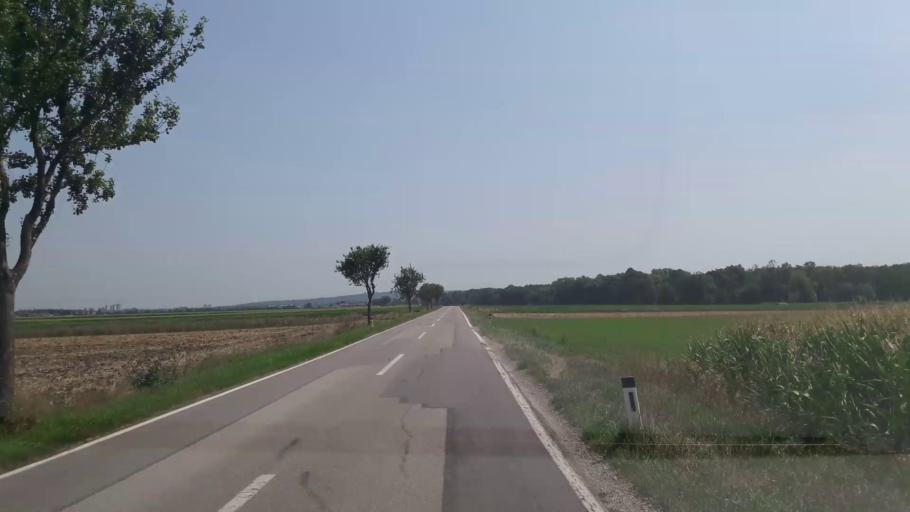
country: AT
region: Lower Austria
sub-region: Politischer Bezirk Bruck an der Leitha
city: Sommerein
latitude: 48.0181
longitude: 16.6977
